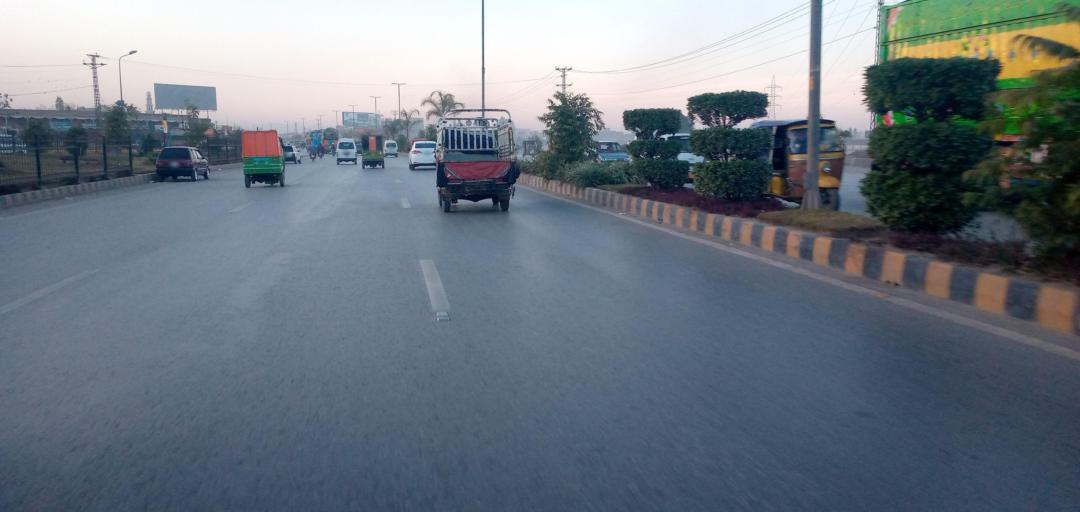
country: PK
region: Khyber Pakhtunkhwa
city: Peshawar
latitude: 34.0265
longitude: 71.6184
